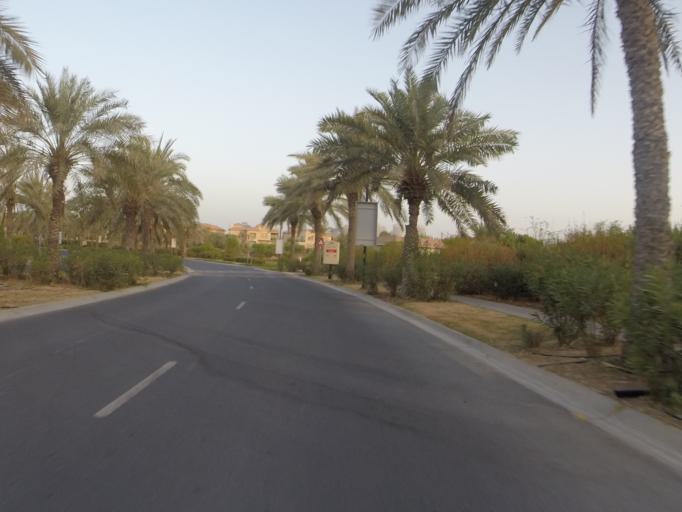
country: AE
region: Dubai
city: Dubai
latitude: 25.0549
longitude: 55.1632
